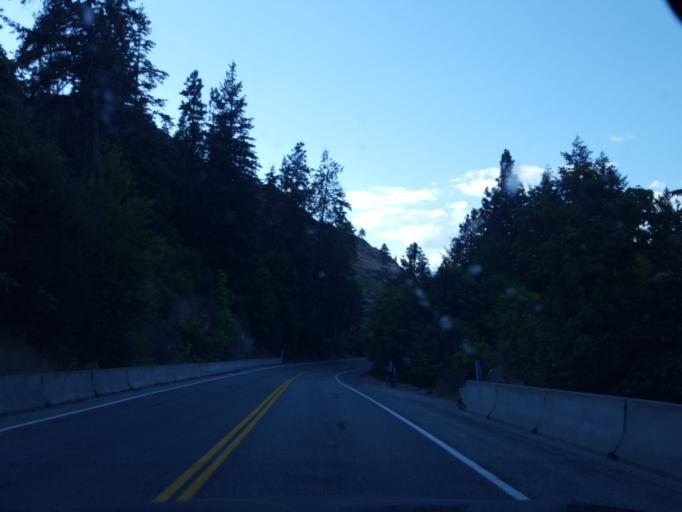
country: US
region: Washington
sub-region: Chelan County
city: Granite Falls
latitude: 47.9639
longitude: -120.2114
